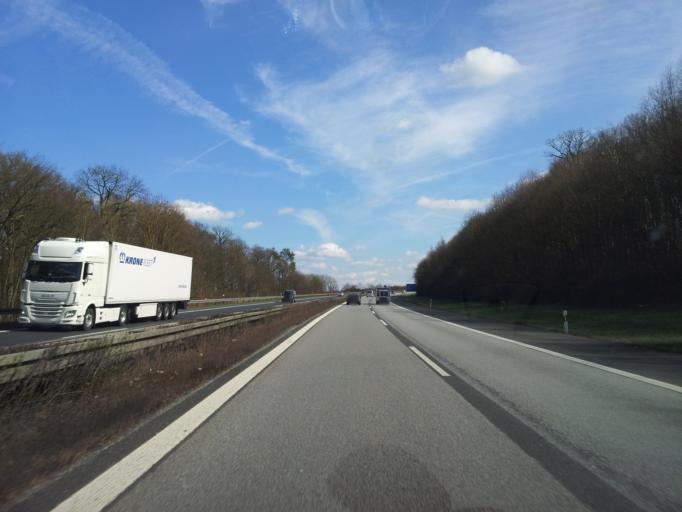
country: DE
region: Bavaria
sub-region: Regierungsbezirk Unterfranken
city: Gadheim
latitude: 50.0187
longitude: 10.3326
